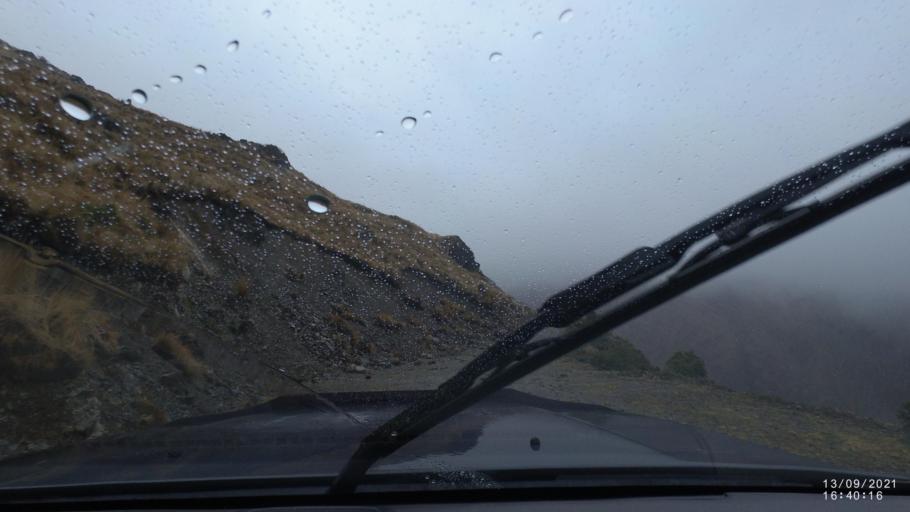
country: BO
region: Cochabamba
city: Colomi
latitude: -17.2809
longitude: -65.7095
